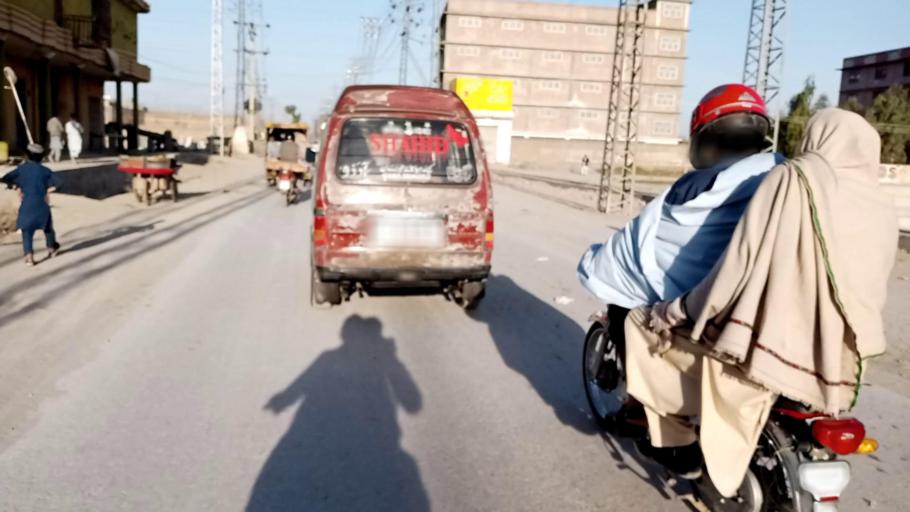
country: PK
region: Khyber Pakhtunkhwa
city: Peshawar
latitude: 34.0499
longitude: 71.6426
